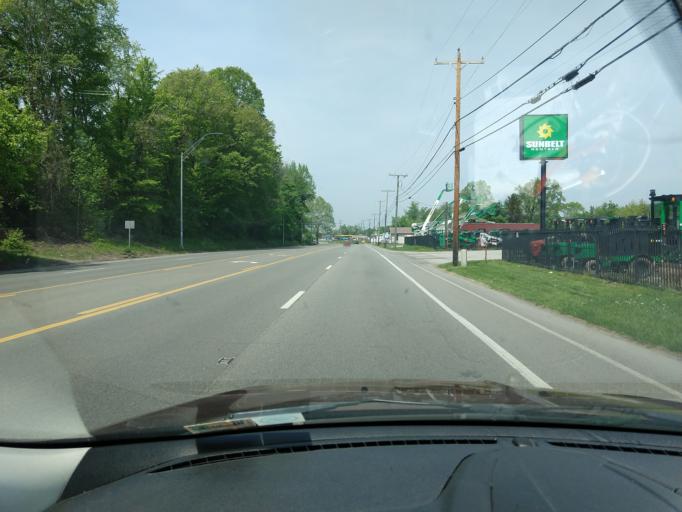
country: US
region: West Virginia
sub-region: Kanawha County
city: Dunbar
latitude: 38.3733
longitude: -81.7745
